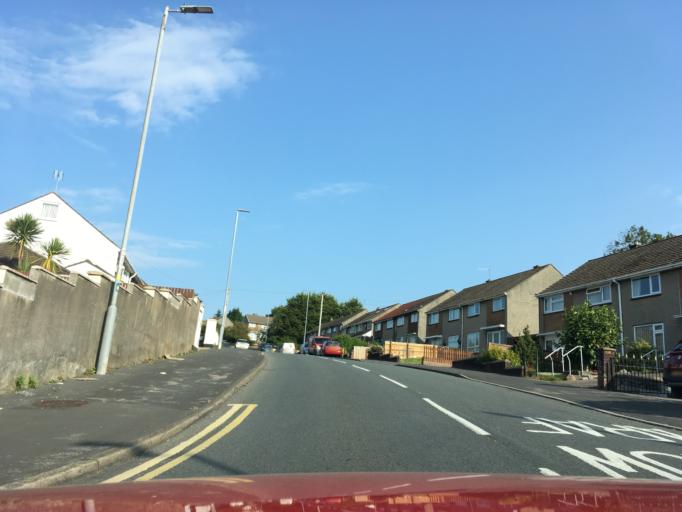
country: GB
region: Wales
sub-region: Newport
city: Newport
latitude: 51.6065
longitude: -3.0330
